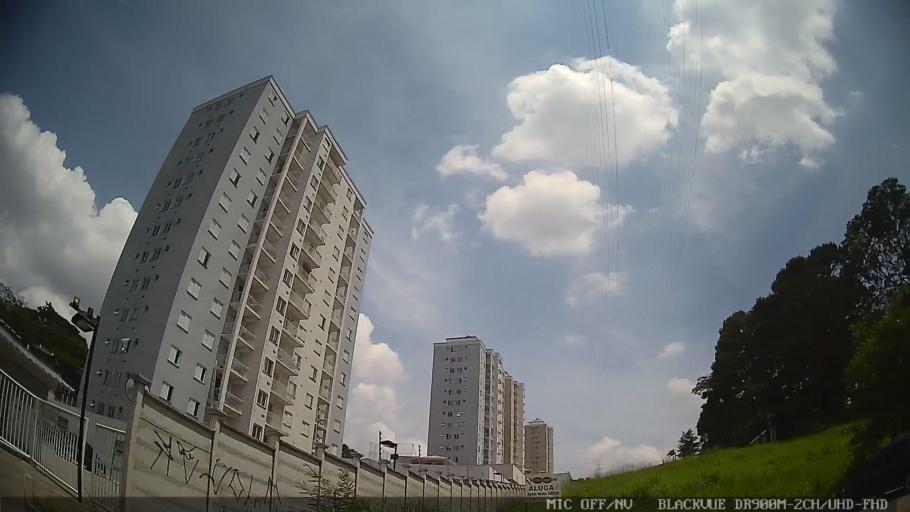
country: BR
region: Sao Paulo
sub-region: Itatiba
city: Itatiba
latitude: -23.0090
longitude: -46.8601
